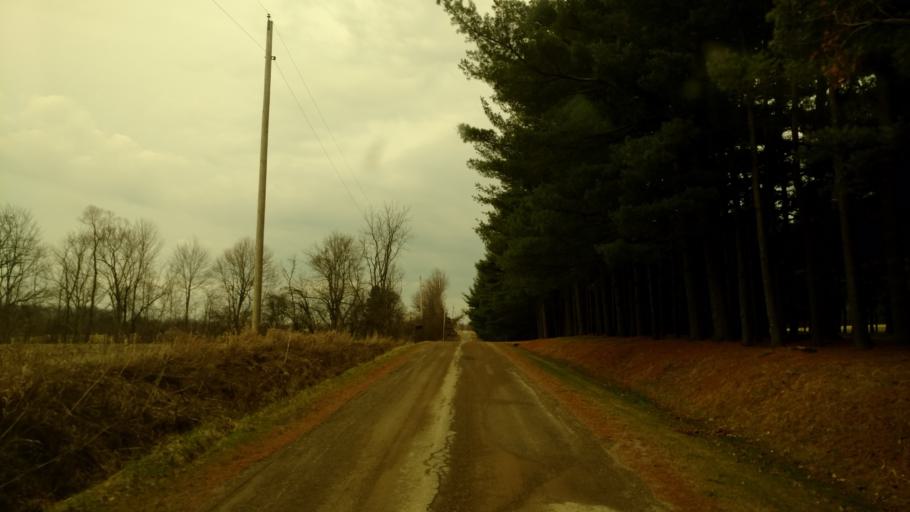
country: US
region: Ohio
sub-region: Richland County
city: Lexington
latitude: 40.6888
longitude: -82.6878
